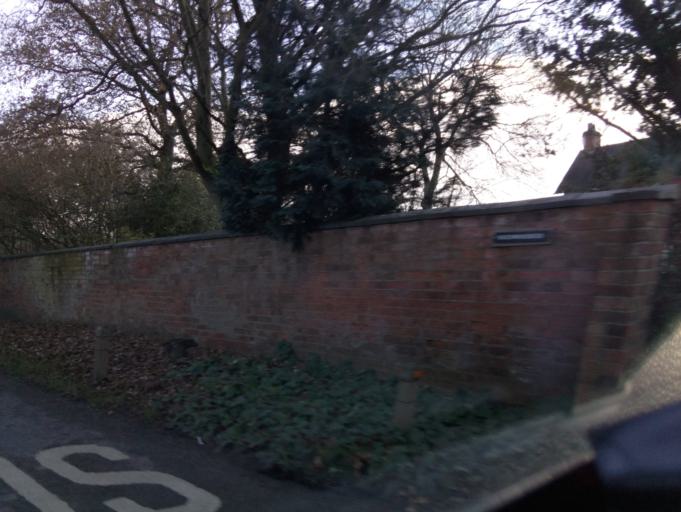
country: GB
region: England
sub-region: Staffordshire
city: Barton under Needwood
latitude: 52.8029
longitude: -1.7239
